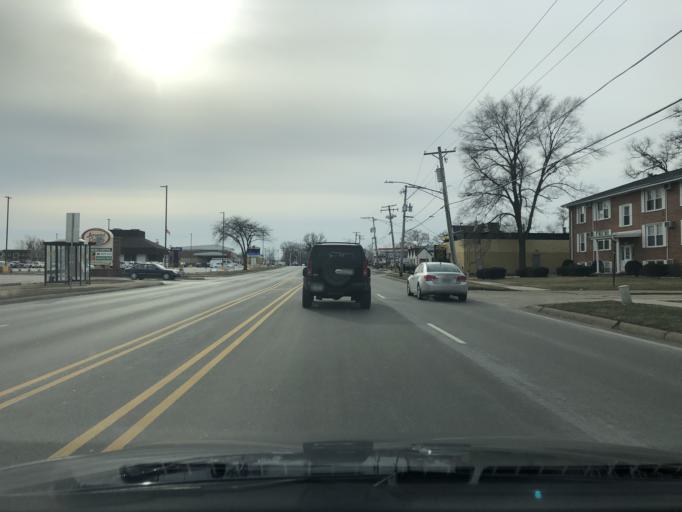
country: US
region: Illinois
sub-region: DuPage County
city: Bensenville
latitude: 41.9338
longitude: -87.9398
